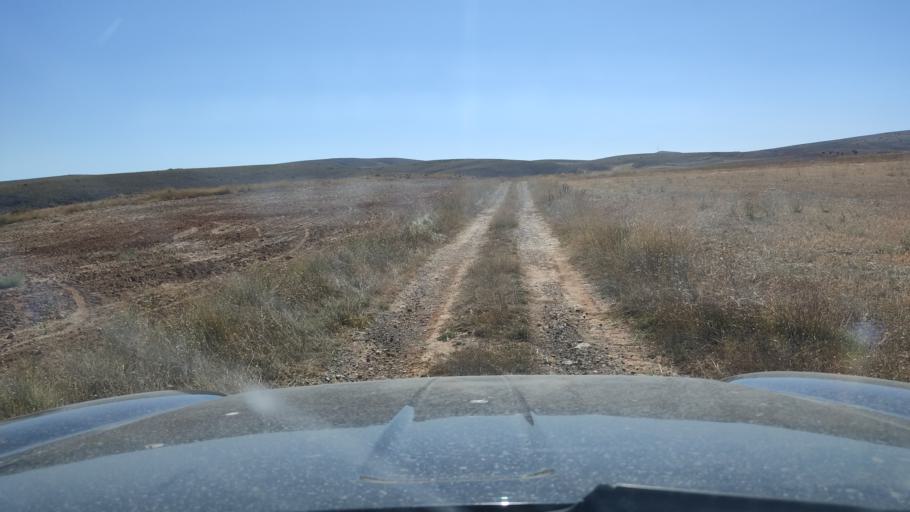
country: ES
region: Aragon
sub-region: Provincia de Teruel
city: Monforte de Moyuela
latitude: 41.0374
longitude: -0.9764
